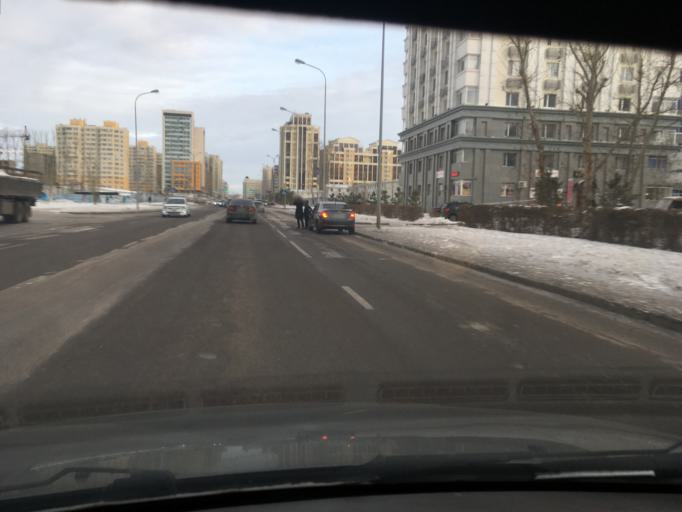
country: KZ
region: Astana Qalasy
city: Astana
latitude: 51.1169
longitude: 71.4224
